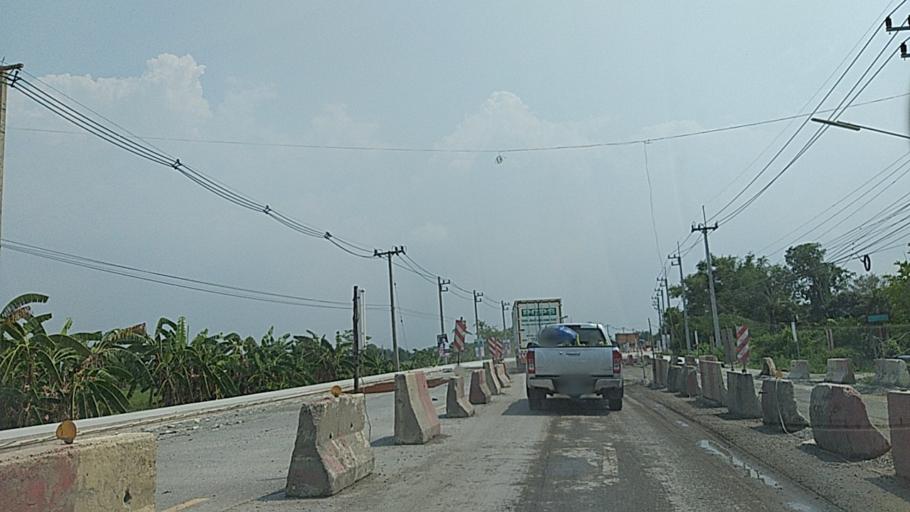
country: TH
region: Chon Buri
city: Phanat Nikhom
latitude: 13.4078
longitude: 101.1898
